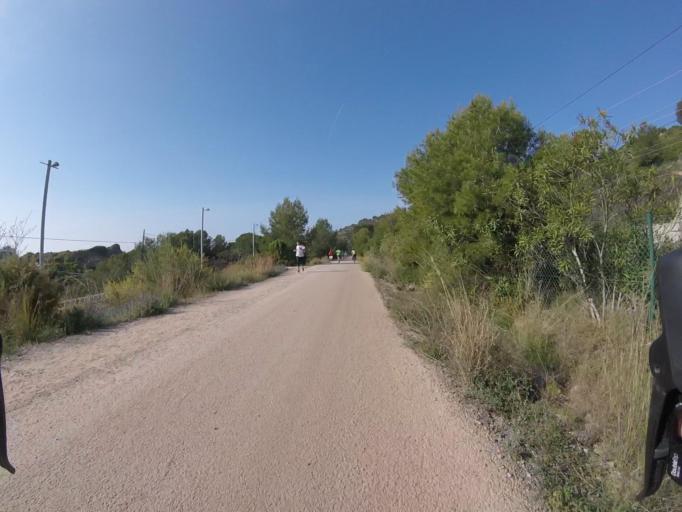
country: ES
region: Valencia
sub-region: Provincia de Castello
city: Orpesa/Oropesa del Mar
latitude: 40.0801
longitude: 0.1349
